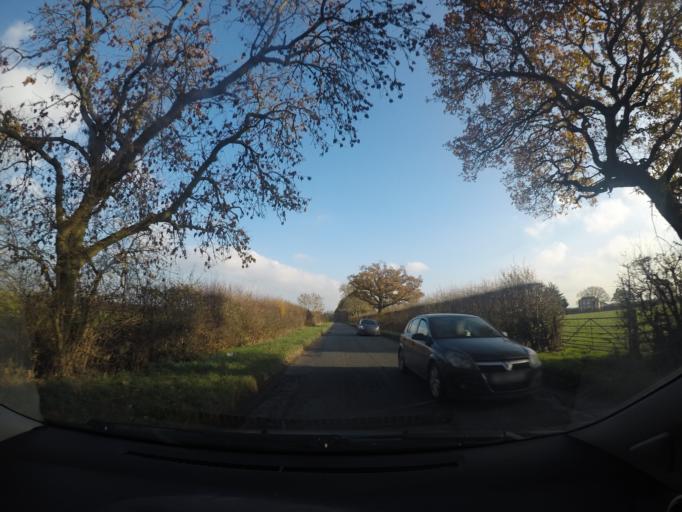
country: GB
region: England
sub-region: City of York
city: Huntington
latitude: 53.9995
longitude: -1.0269
